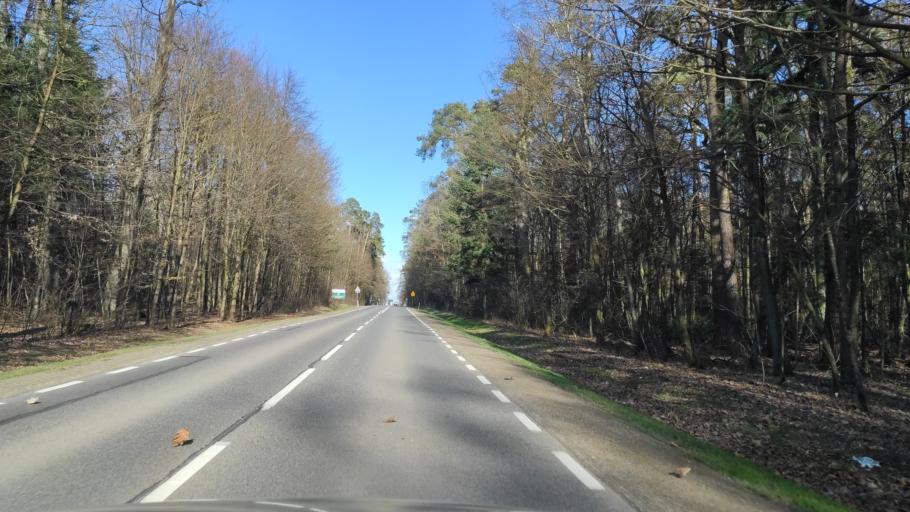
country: PL
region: Masovian Voivodeship
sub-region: Powiat radomski
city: Jedlnia-Letnisko
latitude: 51.4453
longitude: 21.3219
